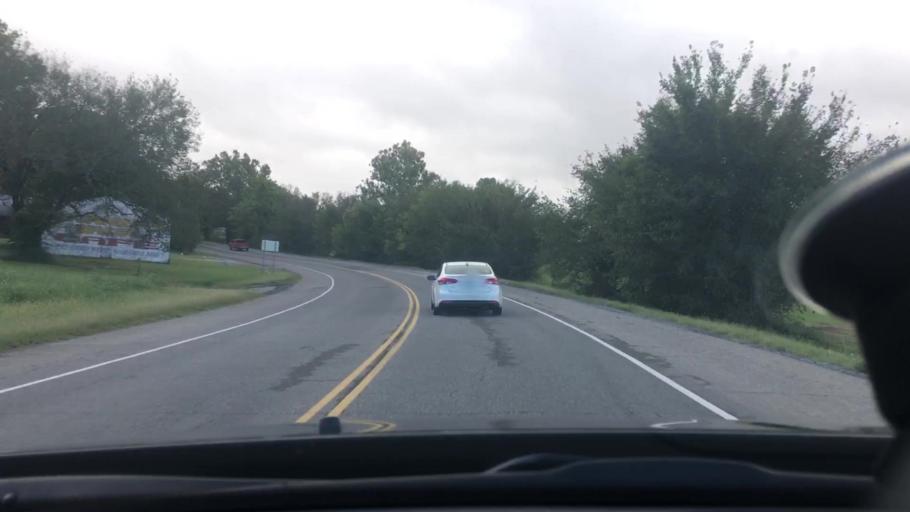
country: US
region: Oklahoma
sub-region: Coal County
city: Coalgate
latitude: 34.5426
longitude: -96.2278
